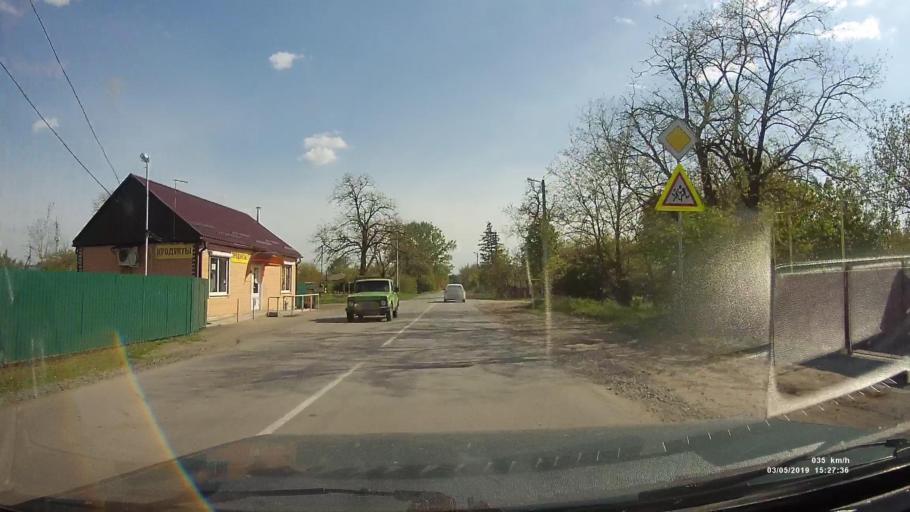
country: RU
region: Rostov
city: Ust'-Donetskiy
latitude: 47.5811
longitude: 40.8417
